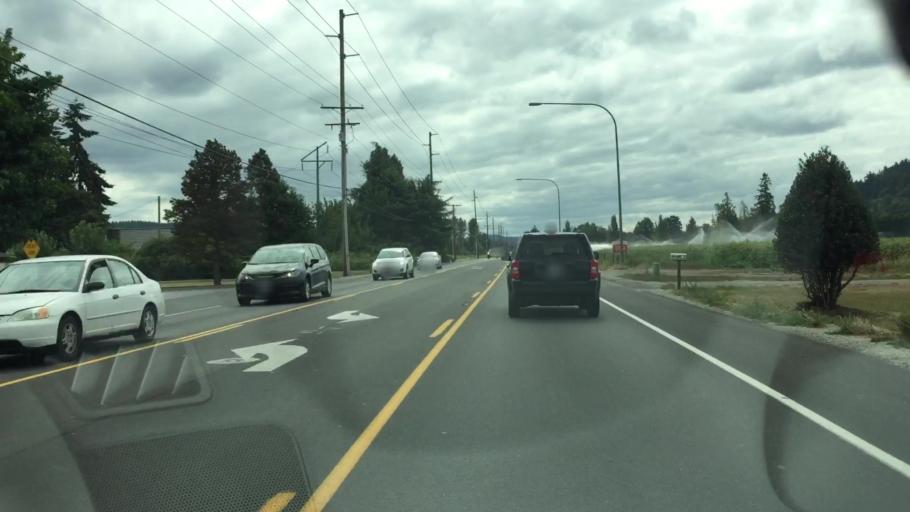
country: US
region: Washington
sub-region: Pierce County
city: Alderton
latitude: 47.1771
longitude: -122.2293
